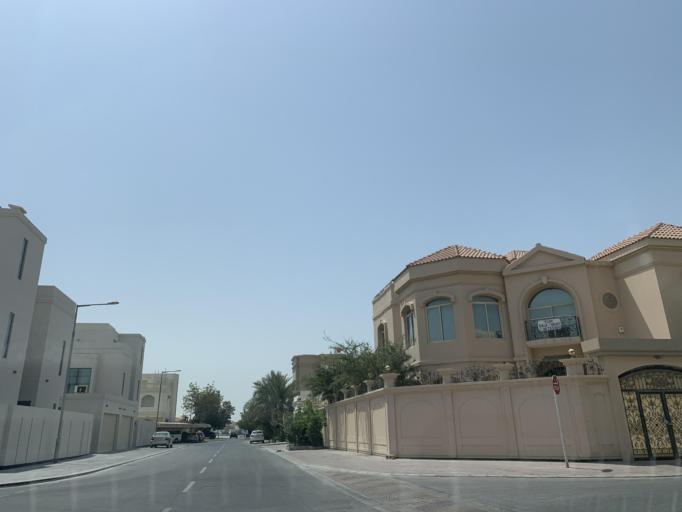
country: BH
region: Manama
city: Manama
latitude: 26.2012
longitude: 50.5655
